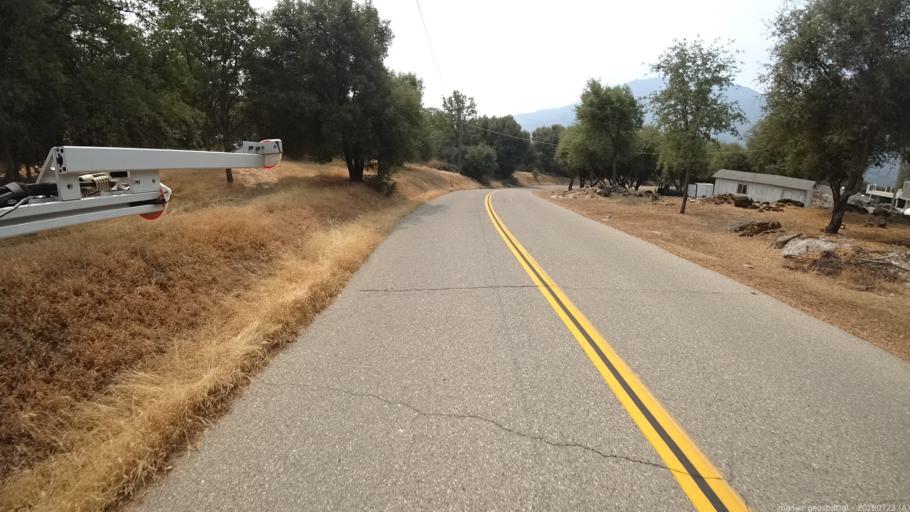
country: US
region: California
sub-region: Madera County
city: Ahwahnee
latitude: 37.3454
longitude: -119.6951
